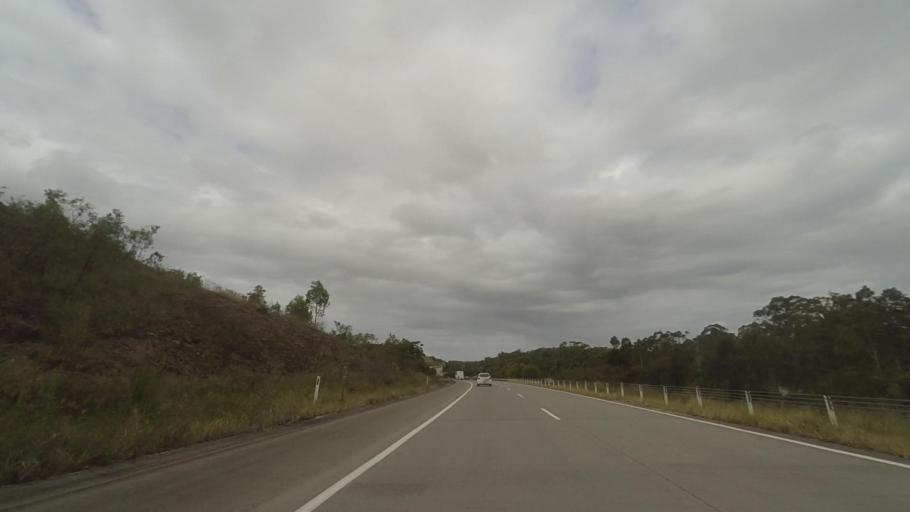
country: AU
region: New South Wales
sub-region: Port Stephens Shire
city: Port Stephens
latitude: -32.6366
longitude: 152.0379
